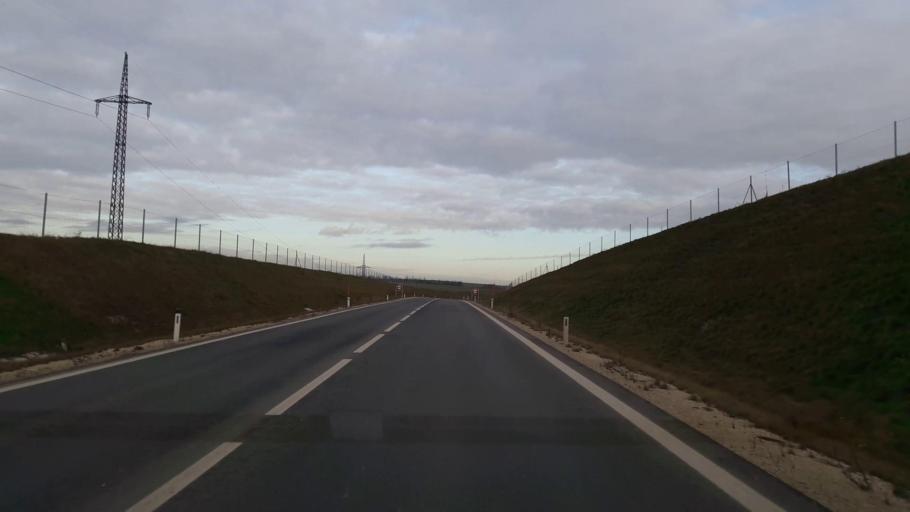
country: AT
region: Lower Austria
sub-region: Politischer Bezirk Mistelbach
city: Mistelbach
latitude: 48.5668
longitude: 16.5541
